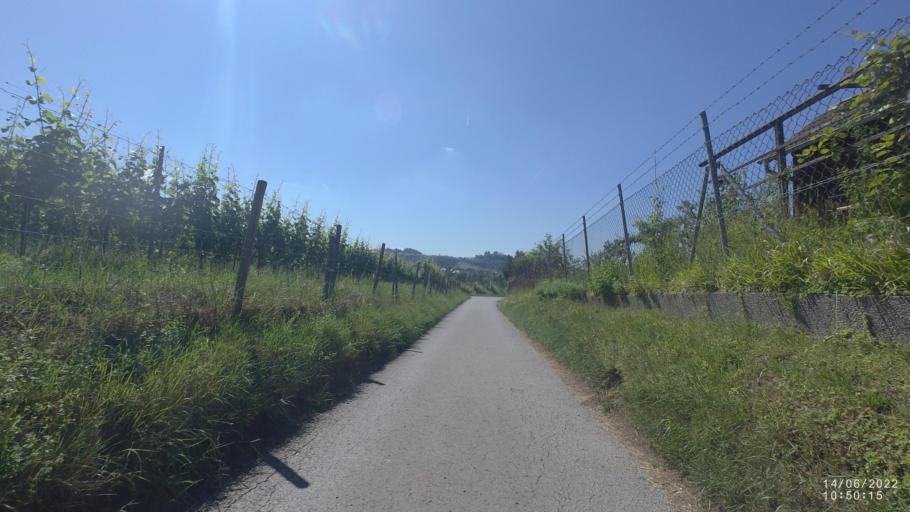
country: DE
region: Baden-Wuerttemberg
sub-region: Regierungsbezirk Stuttgart
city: Fellbach
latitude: 48.8006
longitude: 9.2582
